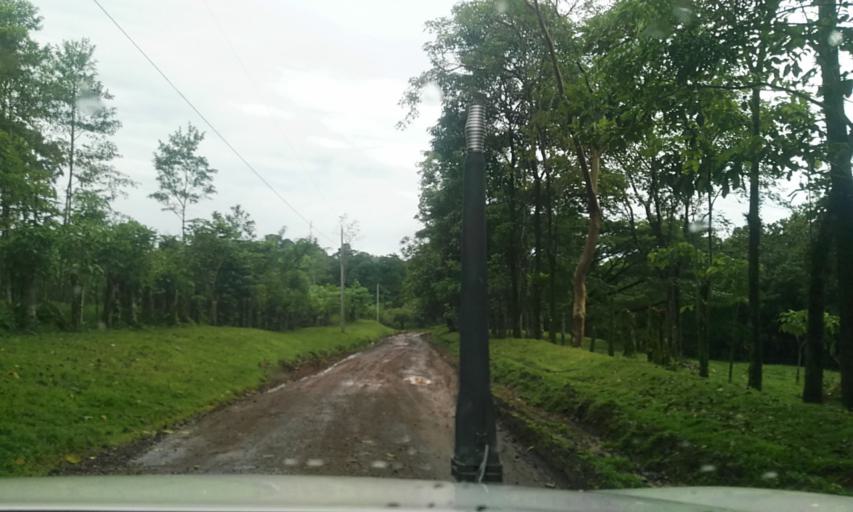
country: NI
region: Matagalpa
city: Rio Blanco
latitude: 12.9591
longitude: -85.1812
